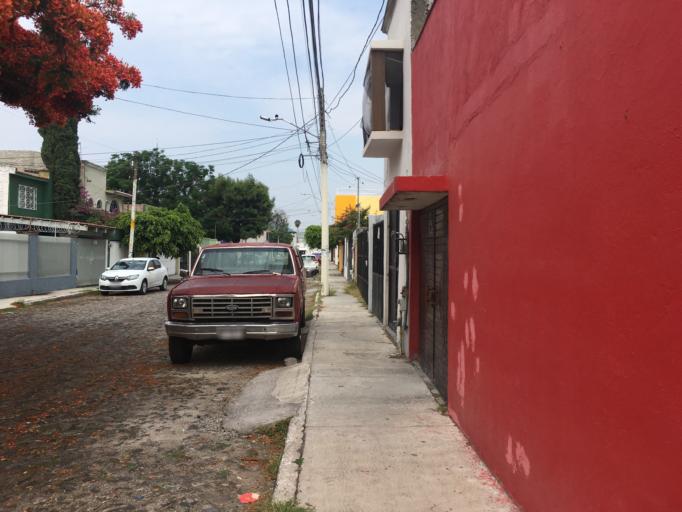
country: MX
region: Queretaro
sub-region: Queretaro
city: Santiago de Queretaro
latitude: 20.6126
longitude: -100.3999
